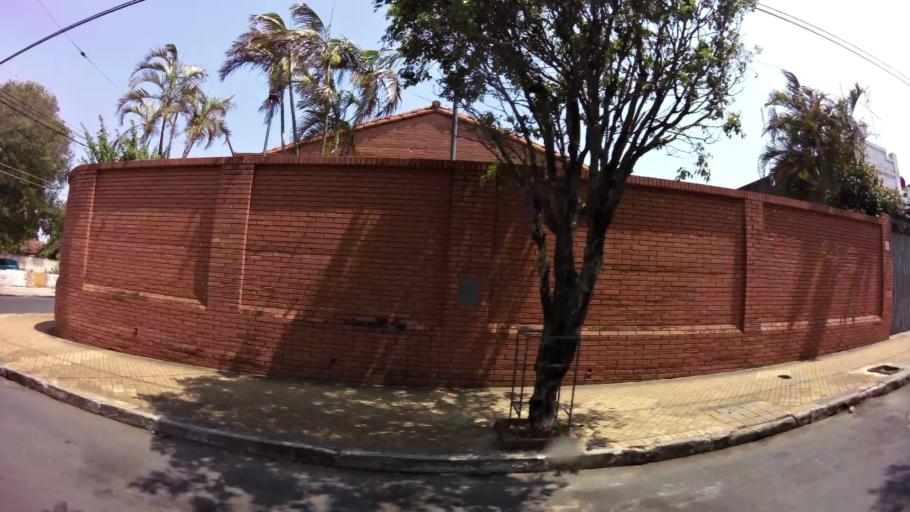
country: PY
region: Asuncion
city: Asuncion
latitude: -25.2915
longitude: -57.6487
